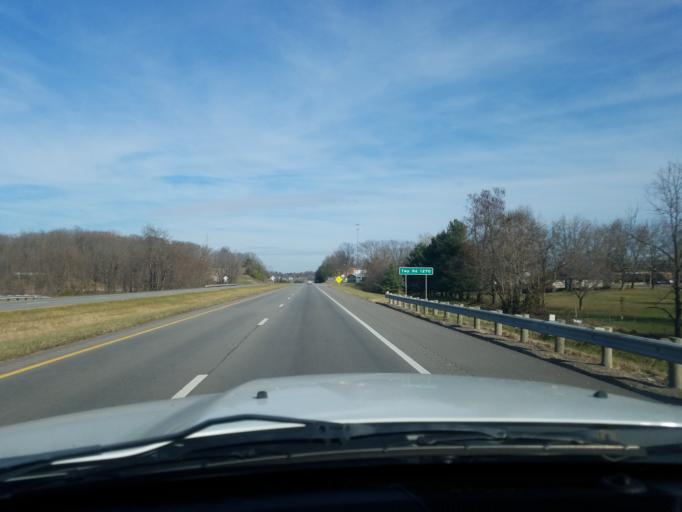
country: US
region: Ohio
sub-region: Athens County
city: Athens
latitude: 39.2416
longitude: -82.1887
